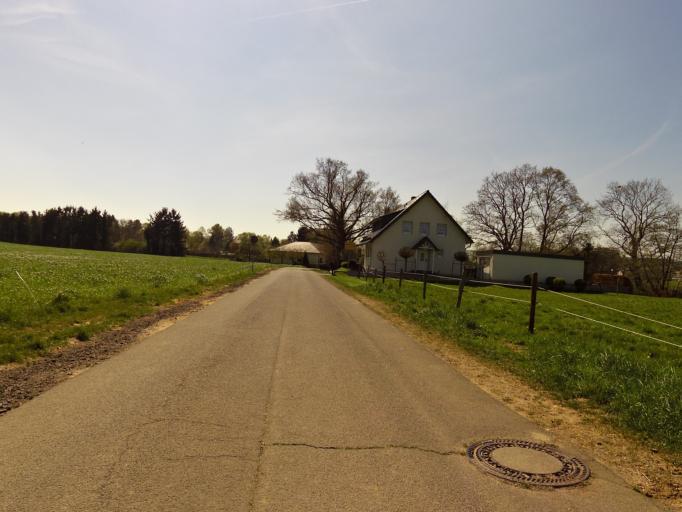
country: DE
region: North Rhine-Westphalia
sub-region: Regierungsbezirk Koln
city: Rheinbach
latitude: 50.6161
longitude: 6.8708
